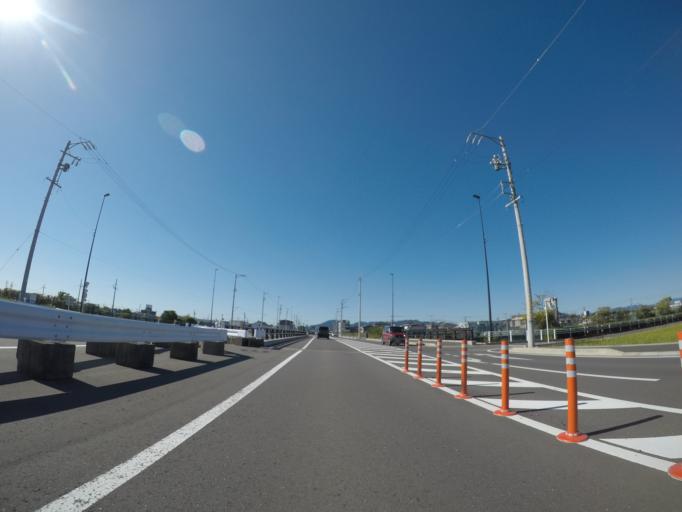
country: JP
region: Shizuoka
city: Shizuoka-shi
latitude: 34.9571
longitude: 138.4229
